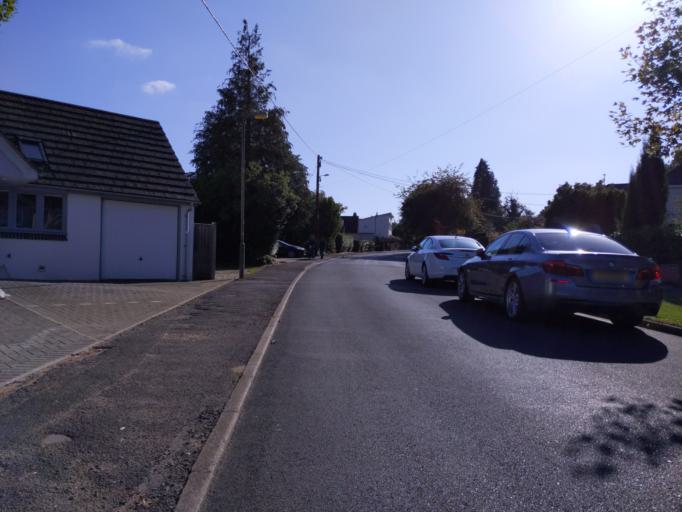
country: GB
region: England
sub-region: Oxfordshire
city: Oxford
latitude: 51.7253
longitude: -1.2507
